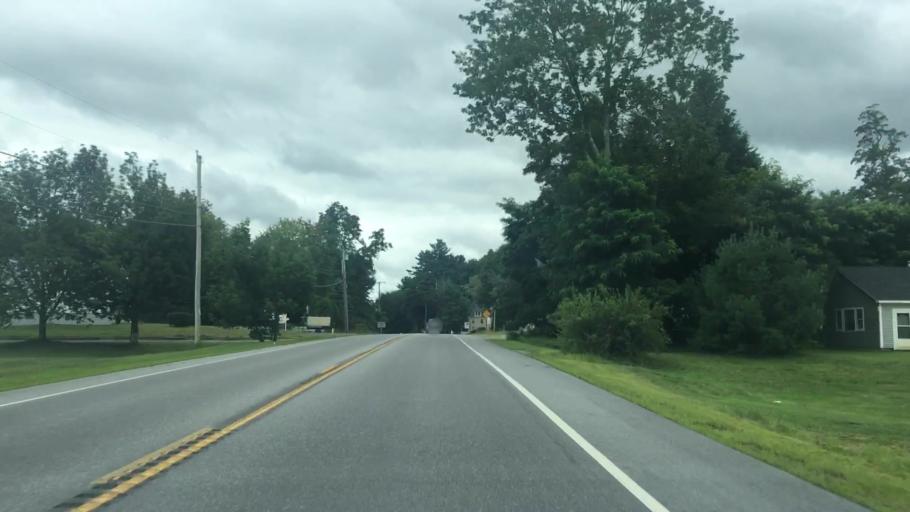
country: US
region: Maine
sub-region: York County
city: Alfred
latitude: 43.4893
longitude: -70.7198
